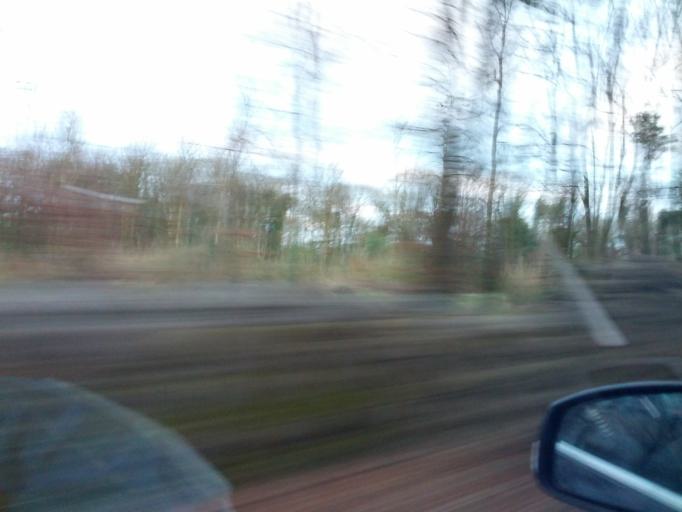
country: IE
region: Connaught
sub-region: County Galway
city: Athenry
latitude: 53.3348
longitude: -8.7705
